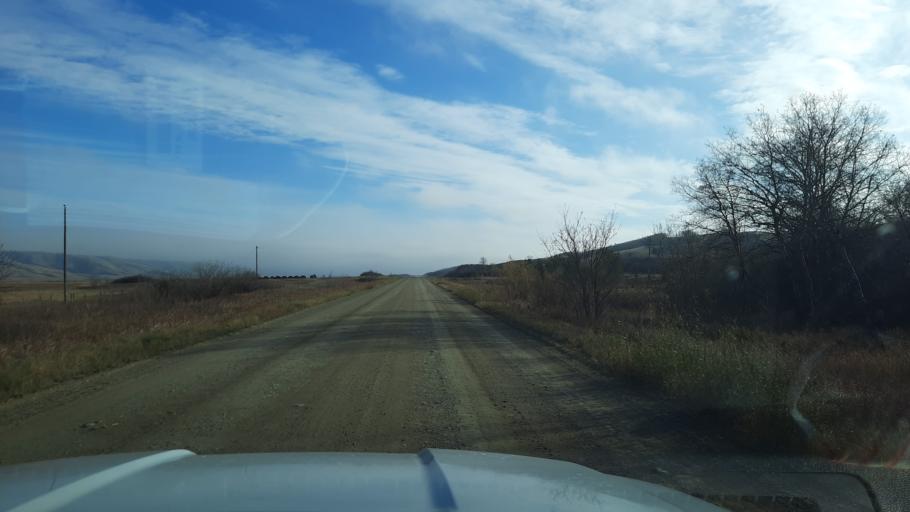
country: CA
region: Saskatchewan
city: Pilot Butte
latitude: 50.7836
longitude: -104.2500
